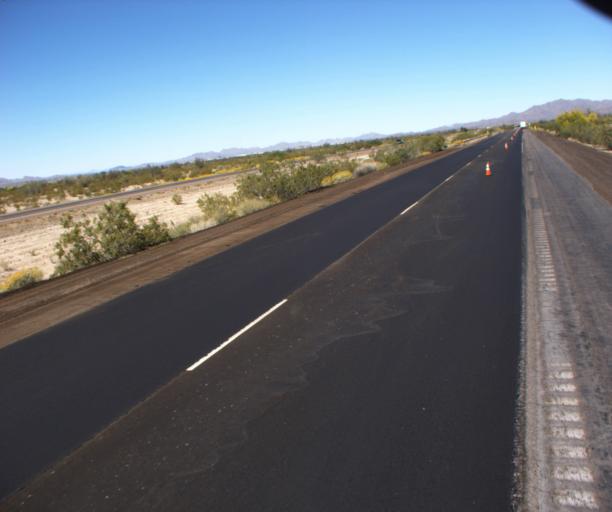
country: US
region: Arizona
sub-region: Maricopa County
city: Gila Bend
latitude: 33.0268
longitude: -112.6483
